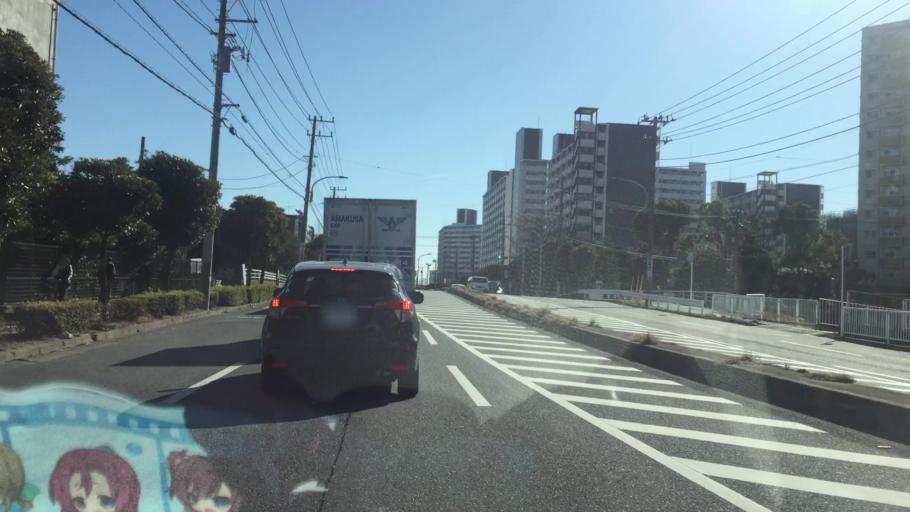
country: JP
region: Tokyo
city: Urayasu
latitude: 35.6652
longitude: 139.9095
